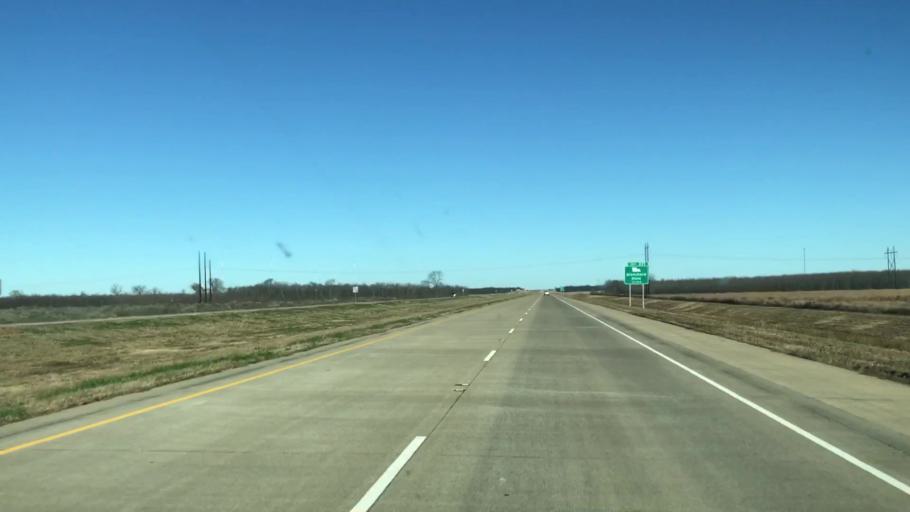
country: US
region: Louisiana
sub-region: Caddo Parish
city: Blanchard
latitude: 32.6627
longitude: -93.8450
